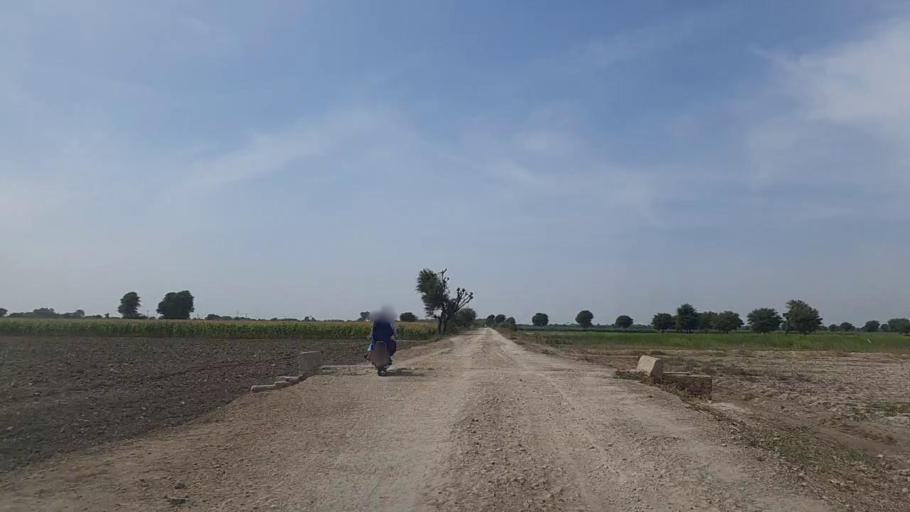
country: PK
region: Sindh
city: Samaro
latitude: 25.2129
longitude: 69.4669
